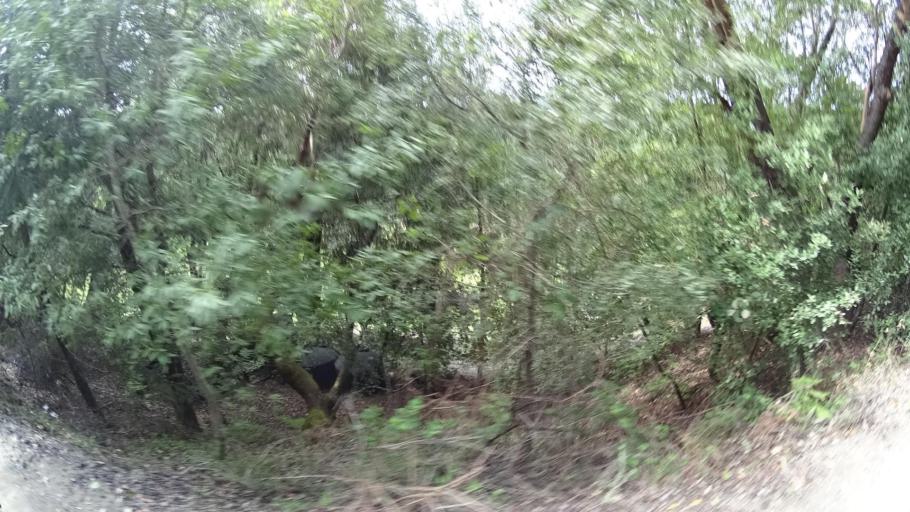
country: US
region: California
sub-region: Humboldt County
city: Redway
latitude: 40.0392
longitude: -123.8434
